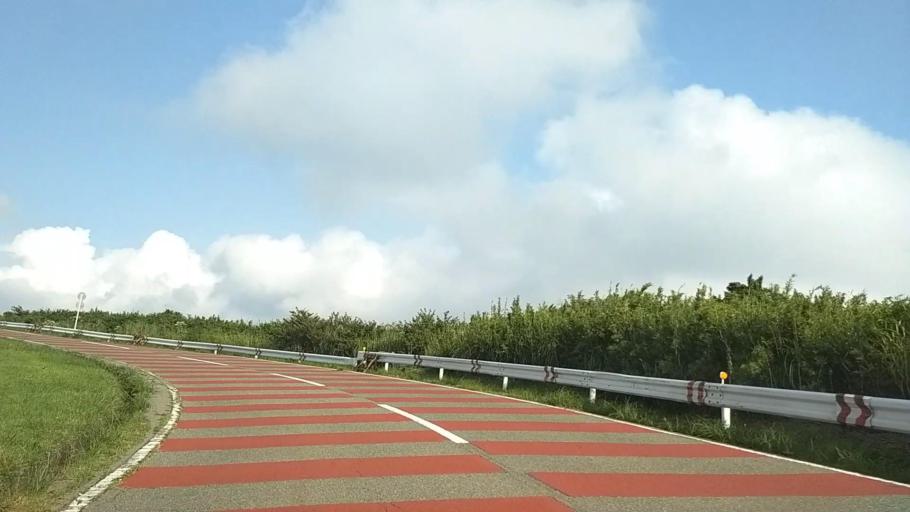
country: JP
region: Kanagawa
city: Hakone
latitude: 35.1971
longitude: 138.9923
